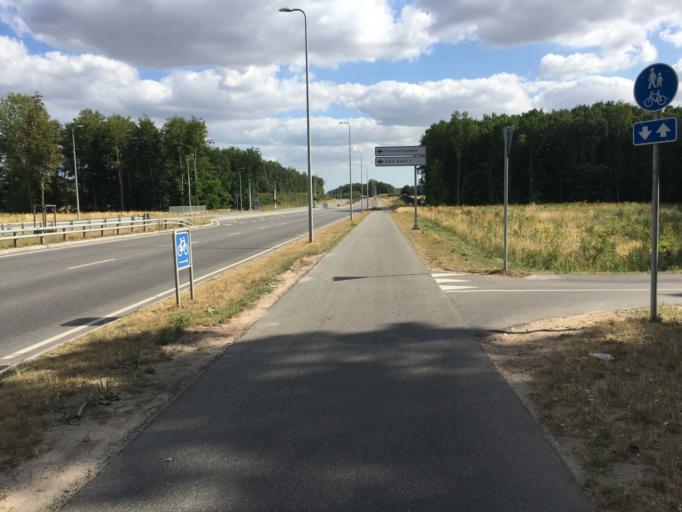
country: DK
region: South Denmark
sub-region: Odense Kommune
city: Odense
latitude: 55.3716
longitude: 10.4096
